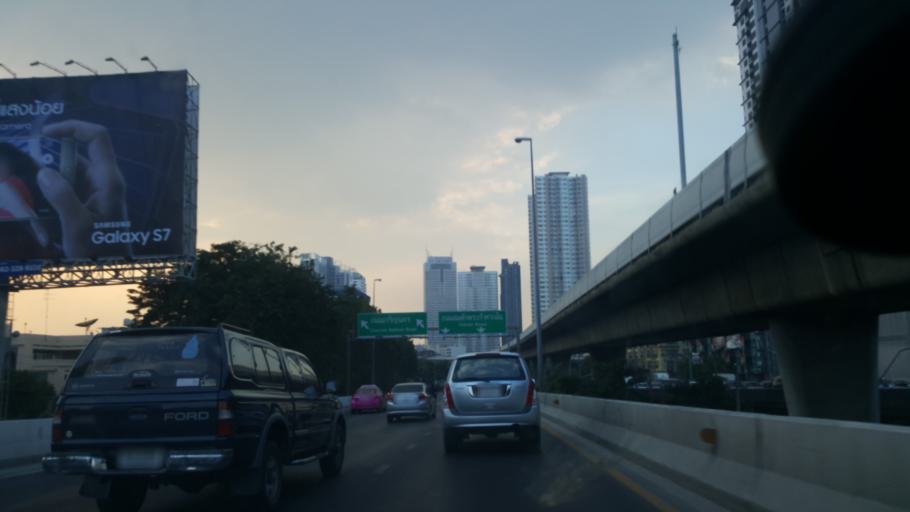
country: TH
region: Bangkok
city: Khlong San
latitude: 13.7201
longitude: 100.5084
